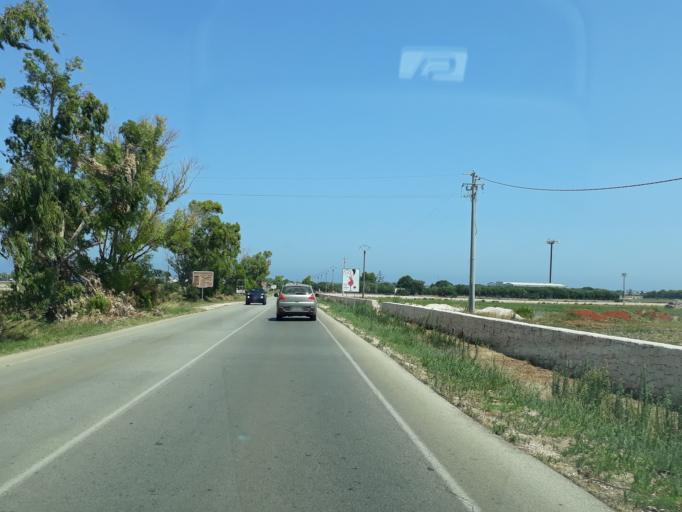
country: IT
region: Apulia
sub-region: Provincia di Brindisi
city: Carovigno
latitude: 40.7456
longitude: 17.6907
